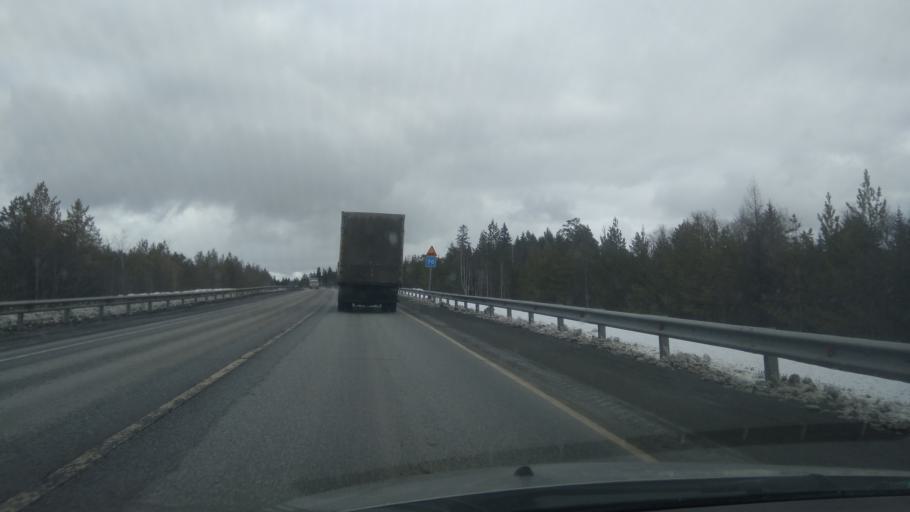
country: RU
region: Sverdlovsk
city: Atig
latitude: 56.7963
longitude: 59.4012
